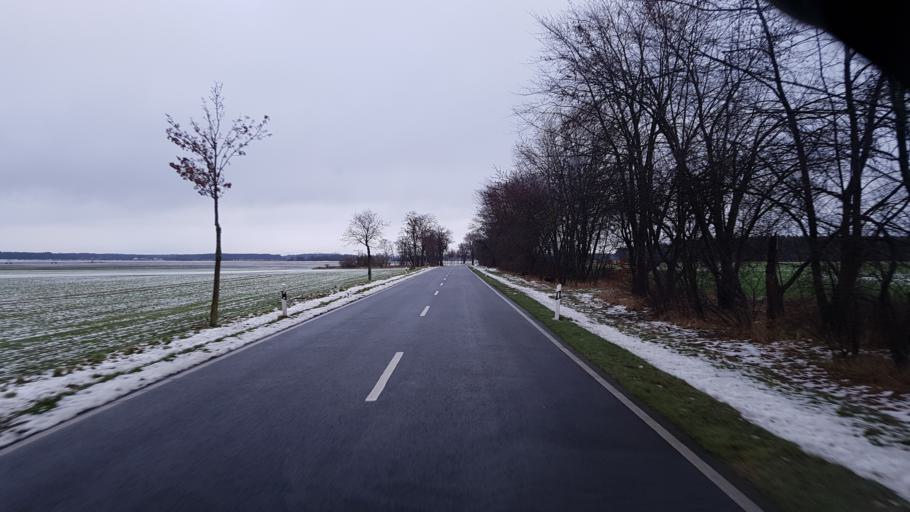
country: DE
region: Brandenburg
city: Luckau
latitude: 51.8500
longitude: 13.7769
